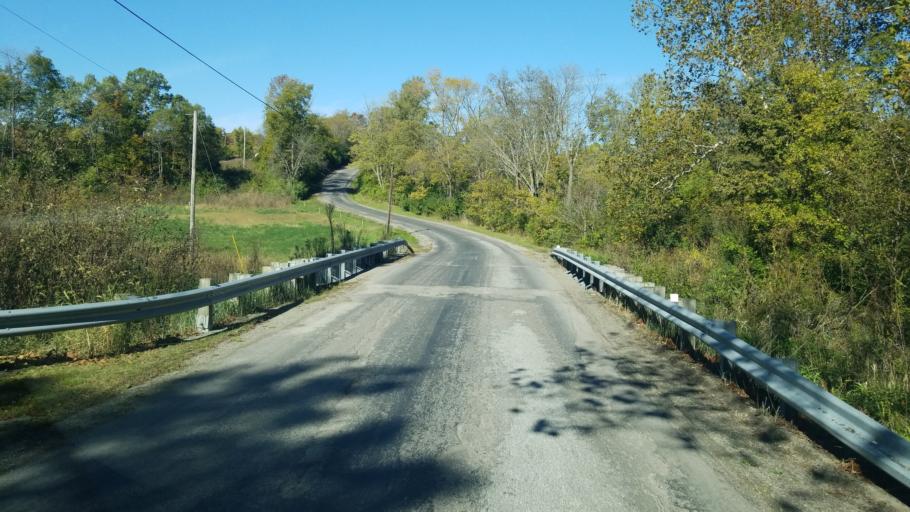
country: US
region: Ohio
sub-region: Highland County
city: Leesburg
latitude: 39.2785
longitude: -83.4714
